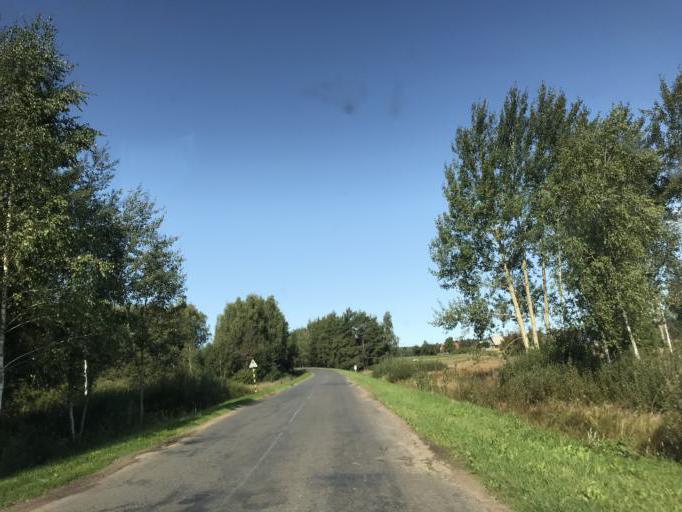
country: BY
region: Mogilev
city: Myazhysyatki
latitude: 53.7960
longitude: 30.1906
